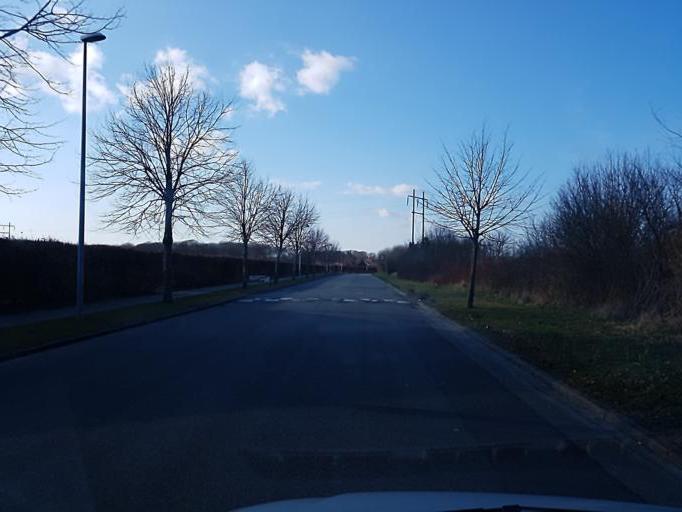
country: DK
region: South Denmark
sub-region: Esbjerg Kommune
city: Bramming
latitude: 55.4805
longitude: 8.7042
